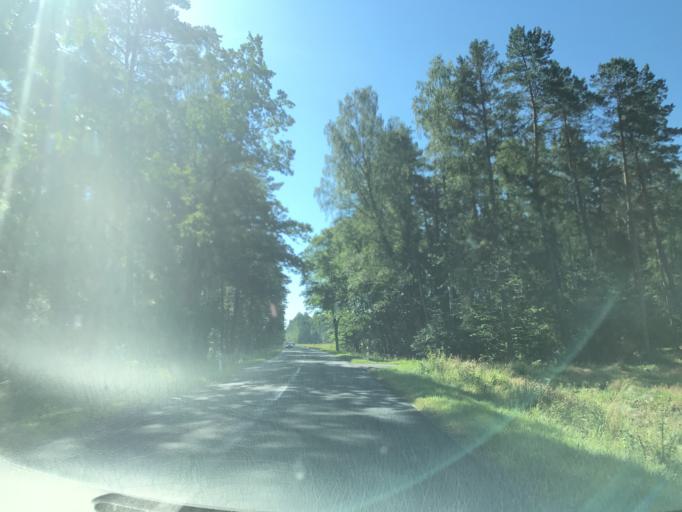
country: PL
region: Pomeranian Voivodeship
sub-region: Powiat slupski
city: Potegowo
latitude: 54.3916
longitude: 17.4737
